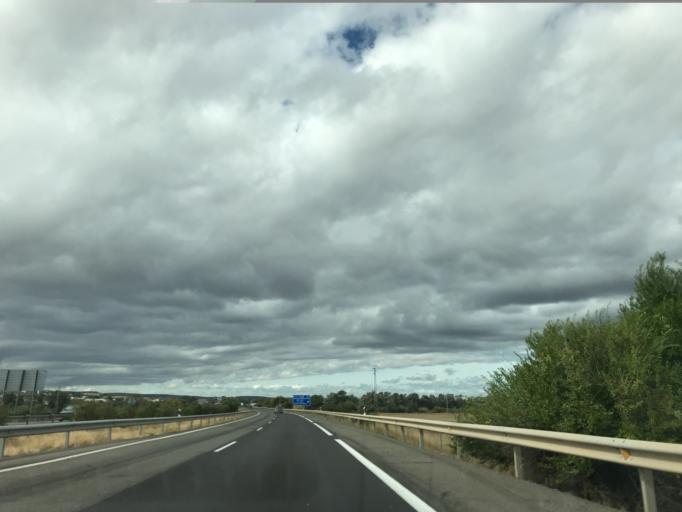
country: ES
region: Andalusia
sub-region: Province of Cordoba
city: Villa del Rio
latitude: 37.9873
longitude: -4.2882
